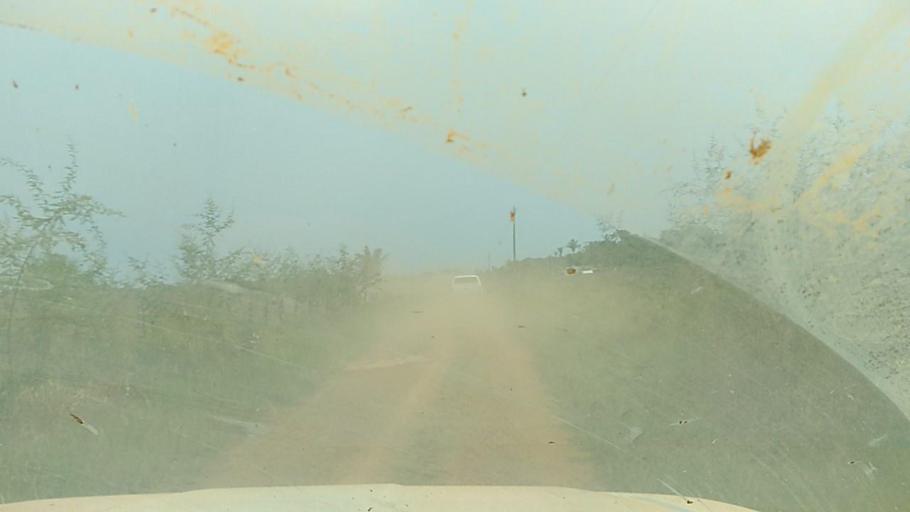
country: BR
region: Rondonia
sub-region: Porto Velho
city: Porto Velho
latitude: -8.9757
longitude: -64.3839
